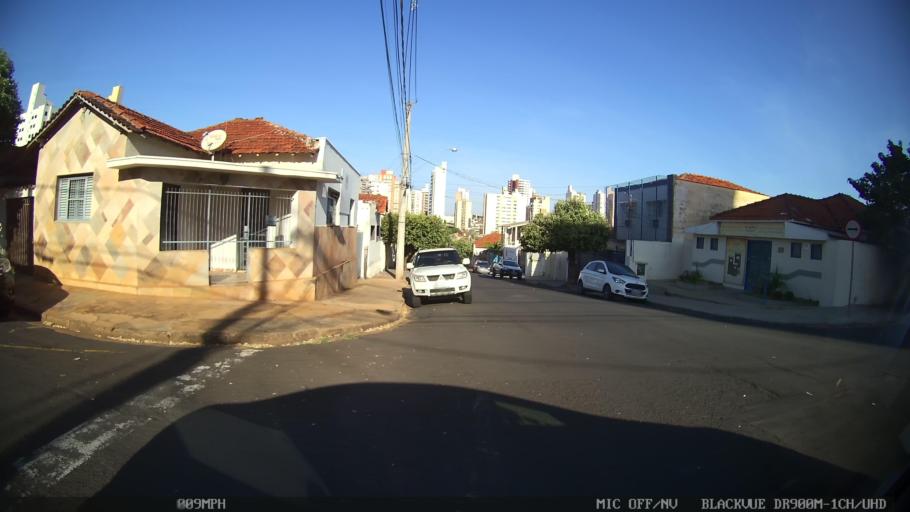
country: BR
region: Sao Paulo
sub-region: Sao Jose Do Rio Preto
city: Sao Jose do Rio Preto
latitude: -20.8116
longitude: -49.3903
